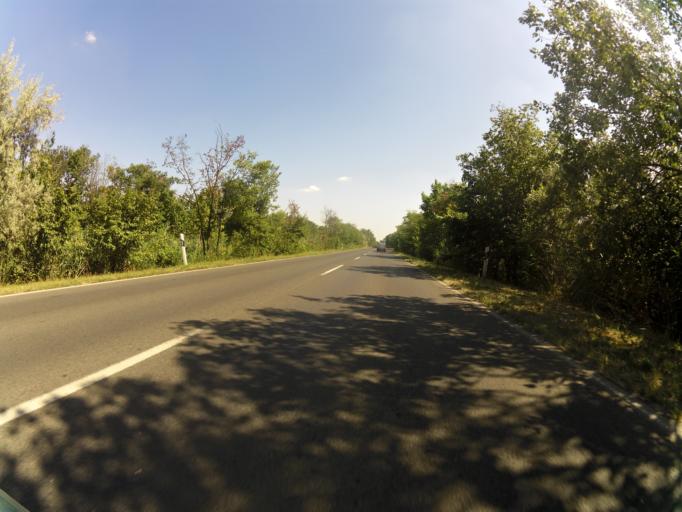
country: HU
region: Csongrad
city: Szatymaz
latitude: 46.3101
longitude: 20.0669
